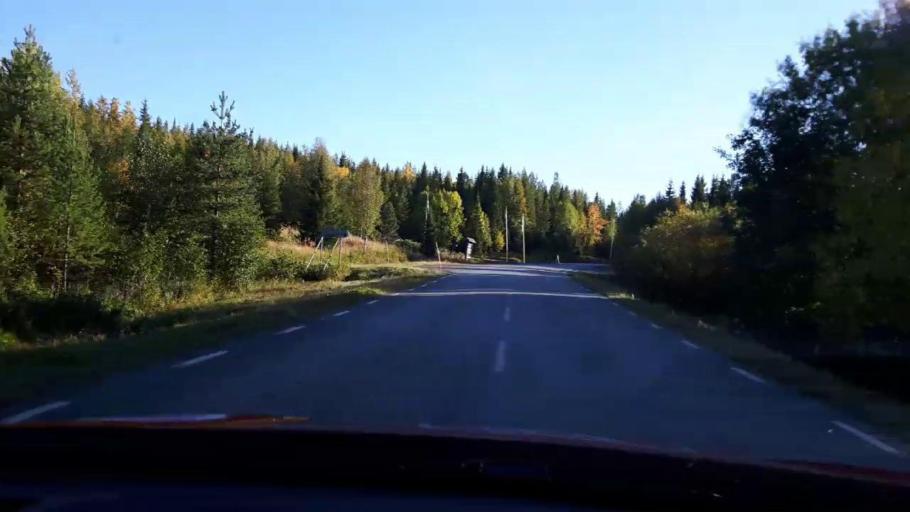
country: SE
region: Jaemtland
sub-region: OEstersunds Kommun
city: Lit
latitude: 63.7984
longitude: 14.7098
